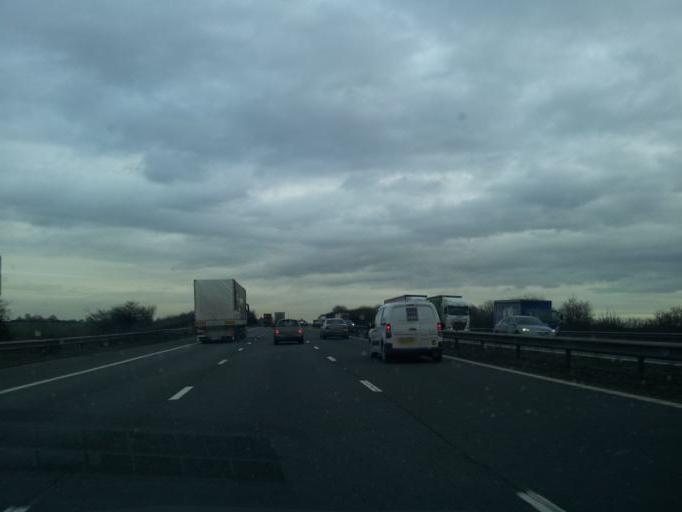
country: GB
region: England
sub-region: Warwickshire
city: Brandon
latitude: 52.4365
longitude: -1.3842
